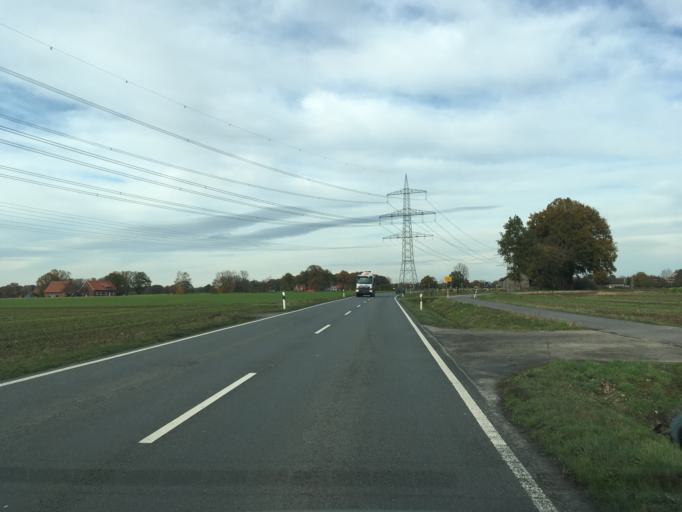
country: DE
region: North Rhine-Westphalia
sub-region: Regierungsbezirk Munster
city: Sudlohn
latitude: 51.8881
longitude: 6.9048
